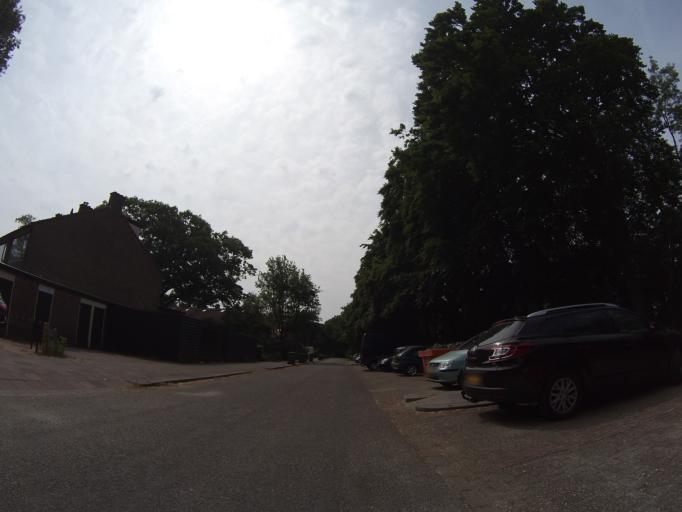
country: NL
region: Utrecht
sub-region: Gemeente Zeist
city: Zeist
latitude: 52.1145
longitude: 5.2808
